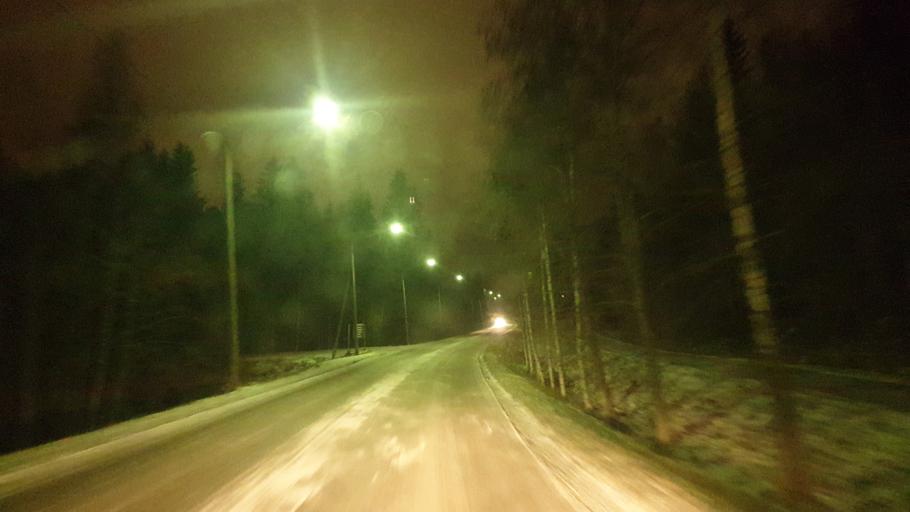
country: FI
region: Southern Savonia
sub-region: Savonlinna
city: Savonlinna
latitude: 61.8615
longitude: 28.9457
